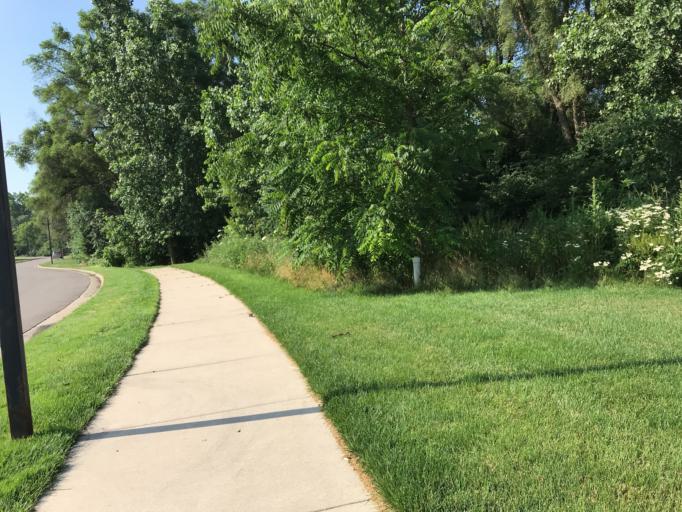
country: US
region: Michigan
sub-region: Washtenaw County
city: Ann Arbor
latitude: 42.2433
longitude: -83.7168
